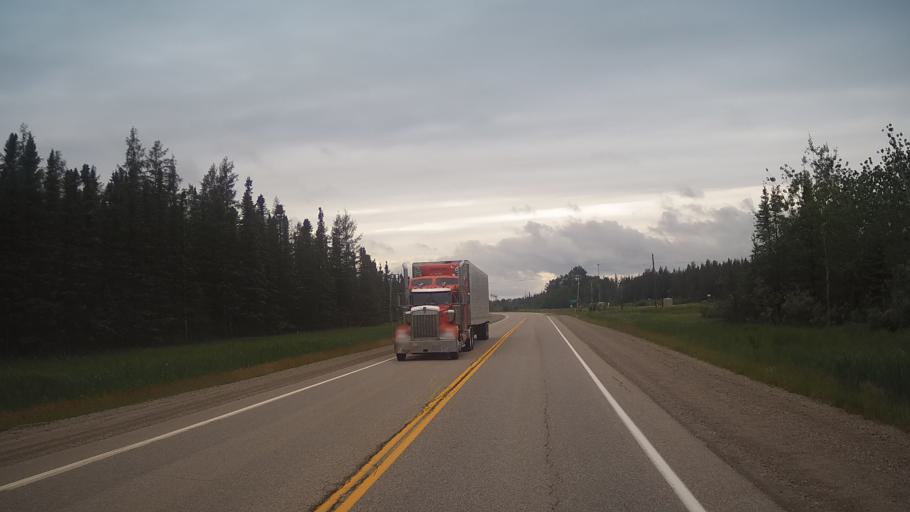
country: CA
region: Ontario
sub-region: Thunder Bay District
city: Thunder Bay
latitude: 48.8899
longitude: -90.0064
